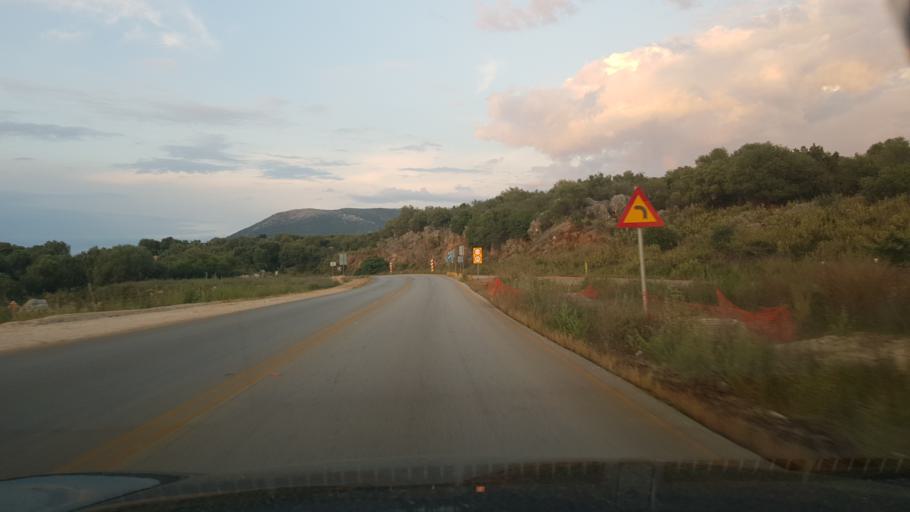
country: GR
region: West Greece
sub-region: Nomos Aitolias kai Akarnanias
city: Vonitsa
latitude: 38.9025
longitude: 20.8767
